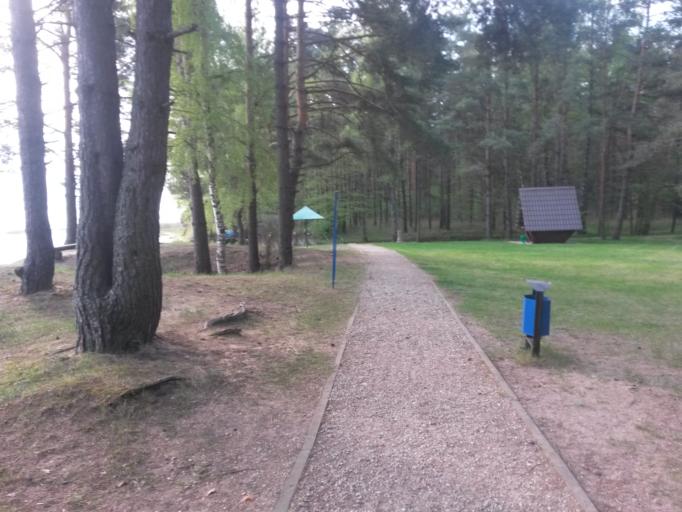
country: BY
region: Minsk
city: Narach
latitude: 54.8315
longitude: 26.7256
